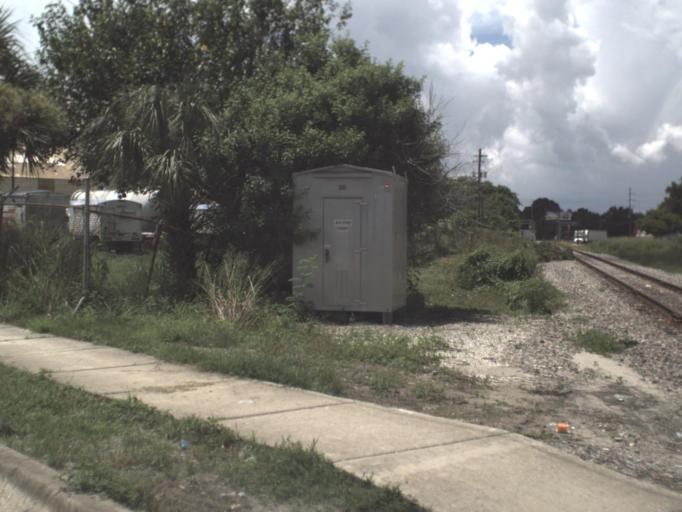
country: US
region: Florida
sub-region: Hillsborough County
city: East Lake-Orient Park
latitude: 27.9834
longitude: -82.4142
